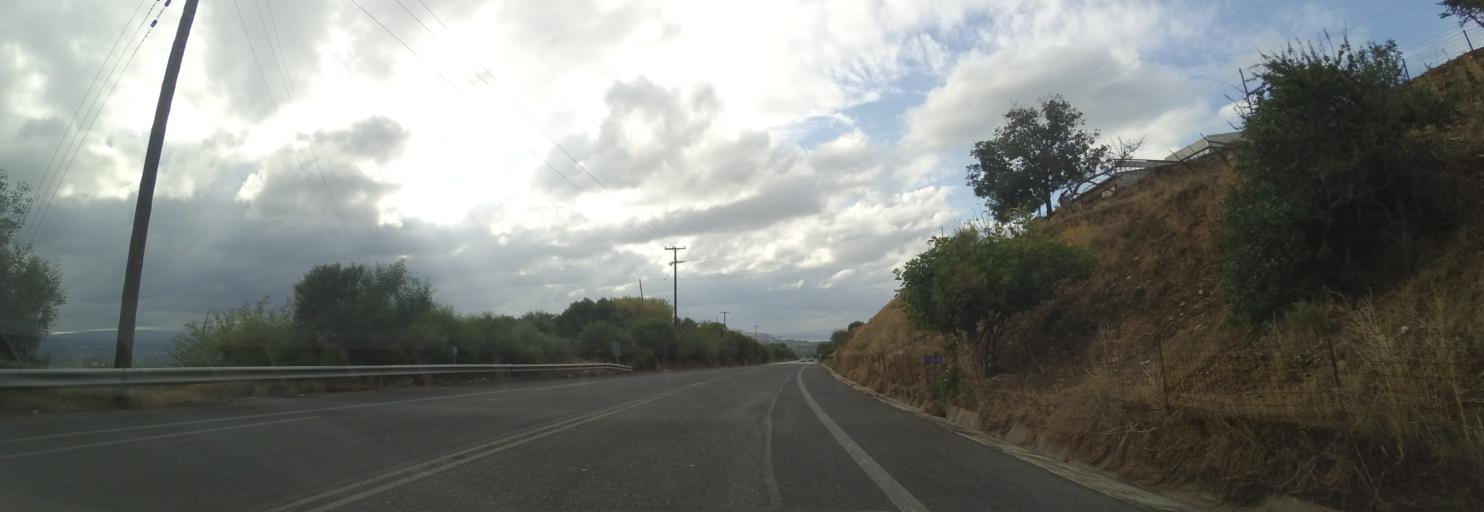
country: GR
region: Crete
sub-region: Nomos Rethymnis
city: Panormos
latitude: 35.4068
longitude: 24.7305
